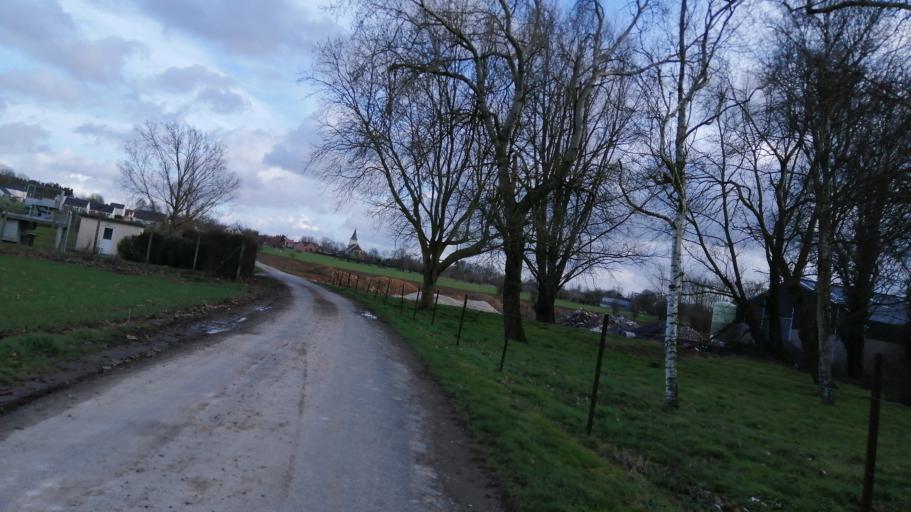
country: FR
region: Nord-Pas-de-Calais
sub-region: Departement du Pas-de-Calais
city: Beaurains
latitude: 50.2399
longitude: 2.7881
